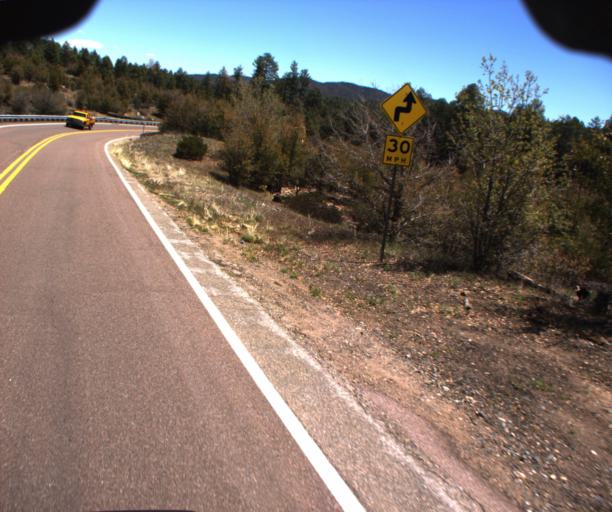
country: US
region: Arizona
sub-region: Yavapai County
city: Prescott
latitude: 34.4944
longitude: -112.4921
